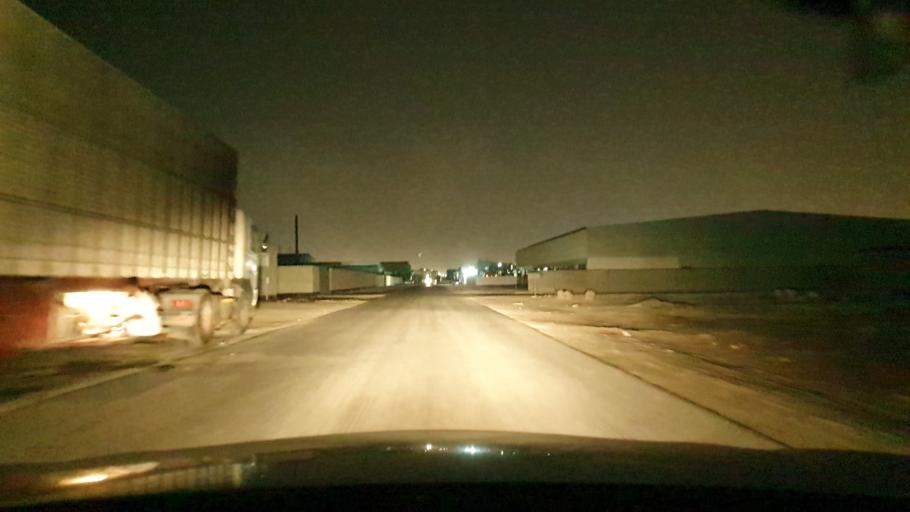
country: BH
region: Northern
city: Sitrah
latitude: 26.0973
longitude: 50.6247
